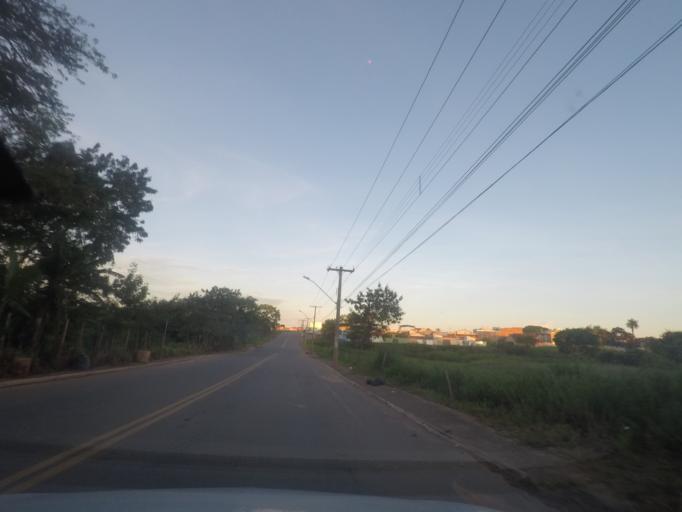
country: BR
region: Goias
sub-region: Goiania
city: Goiania
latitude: -16.6898
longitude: -49.3410
